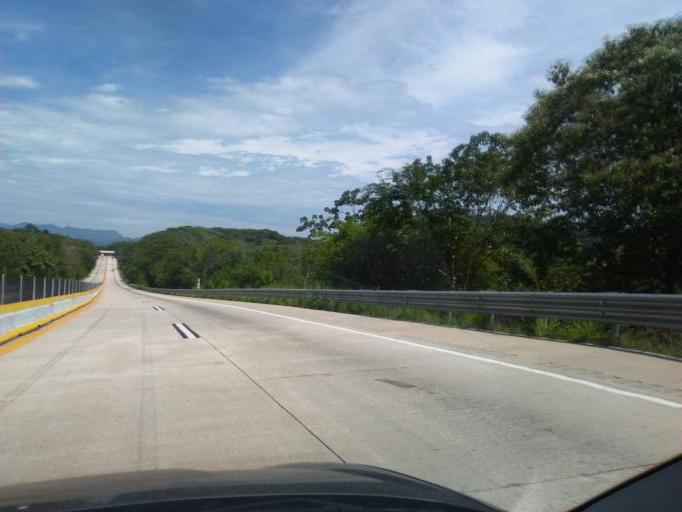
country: MX
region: Guerrero
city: Xaltianguis
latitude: 17.0053
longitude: -99.6688
